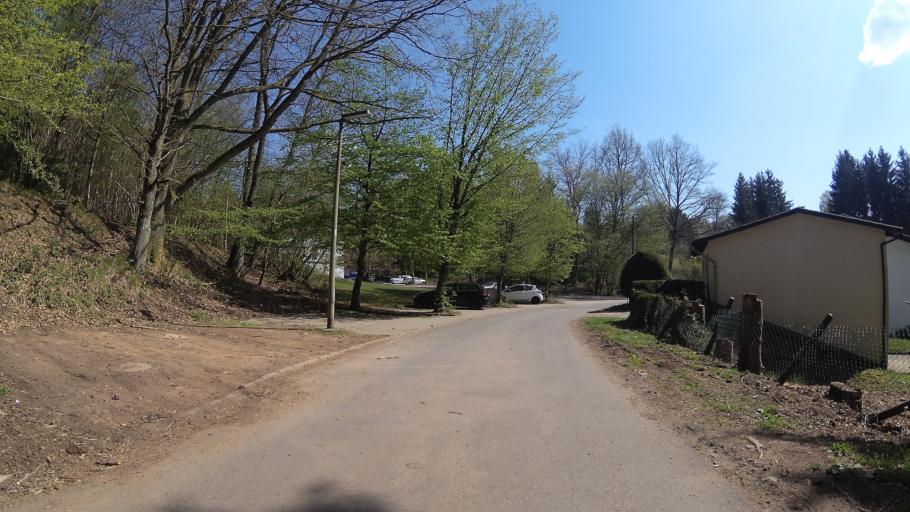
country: DE
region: Saarland
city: Ottweiler
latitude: 49.4145
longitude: 7.1917
